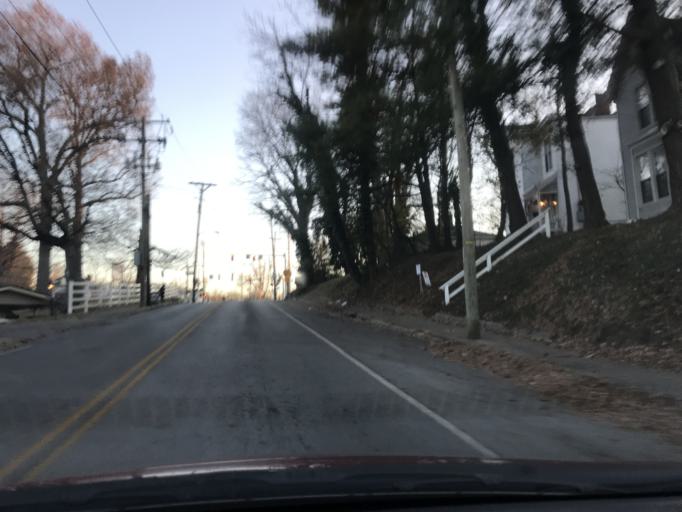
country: US
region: Kentucky
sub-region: Jefferson County
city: Indian Hills
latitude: 38.2547
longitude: -85.7003
